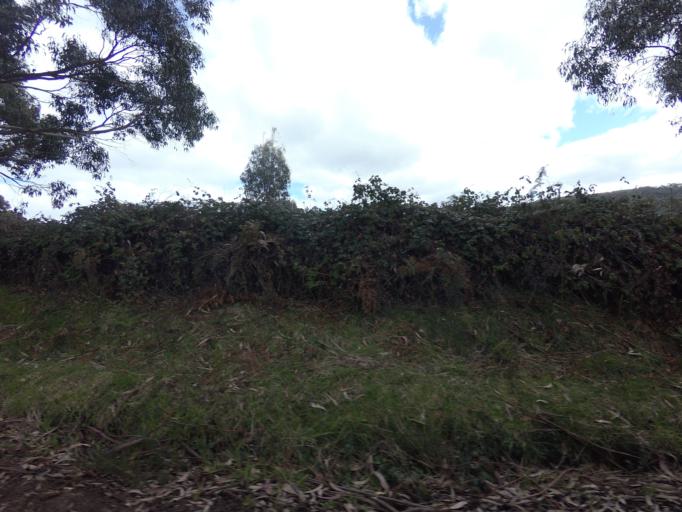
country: AU
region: Tasmania
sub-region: Huon Valley
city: Cygnet
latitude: -43.4102
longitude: 147.0191
